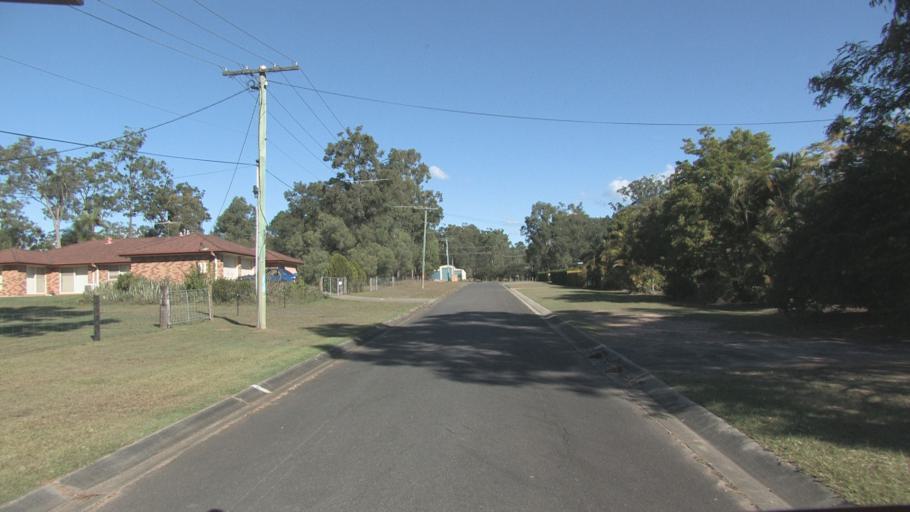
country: AU
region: Queensland
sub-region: Logan
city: Park Ridge South
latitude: -27.6980
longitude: 153.0284
